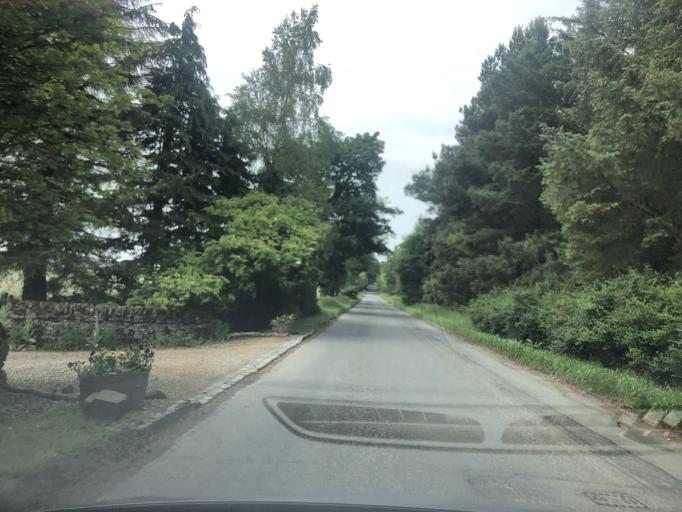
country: GB
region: Scotland
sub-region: The Scottish Borders
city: West Linton
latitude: 55.7354
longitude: -3.3318
